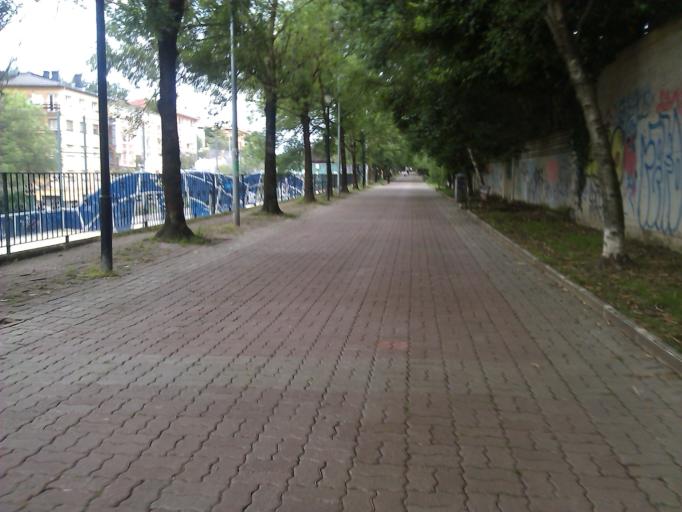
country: ES
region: Basque Country
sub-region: Provincia de Guipuzcoa
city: Pasaia
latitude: 43.3191
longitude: -1.9475
